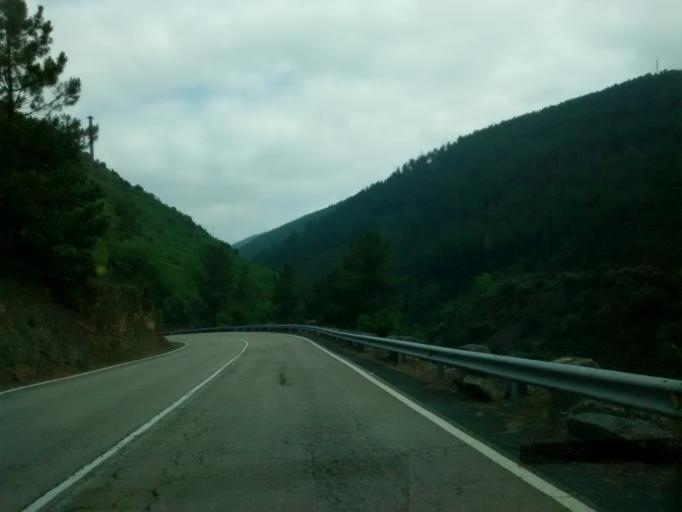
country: ES
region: Galicia
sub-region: Provincia de Ourense
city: Manzaneda
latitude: 42.3293
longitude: -7.2140
